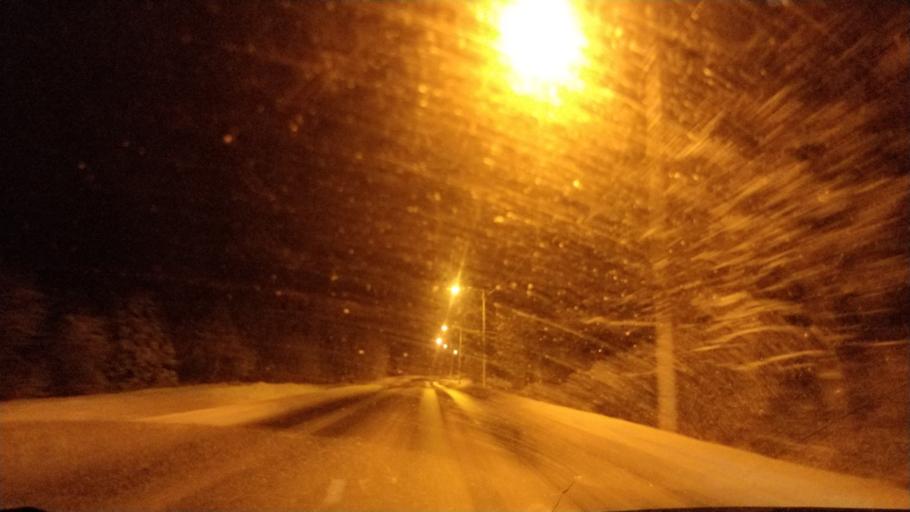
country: FI
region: Lapland
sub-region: Rovaniemi
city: Rovaniemi
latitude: 66.4009
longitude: 25.3886
